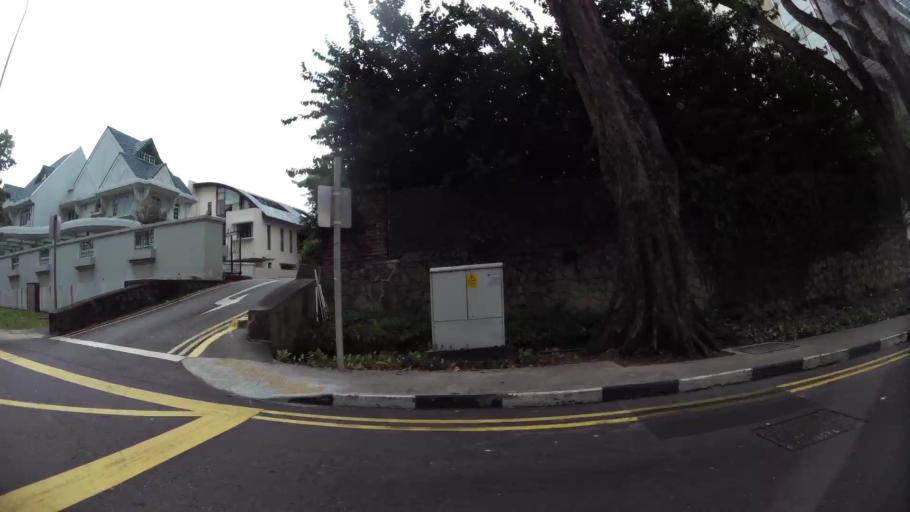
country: SG
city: Singapore
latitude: 1.3020
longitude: 103.8295
